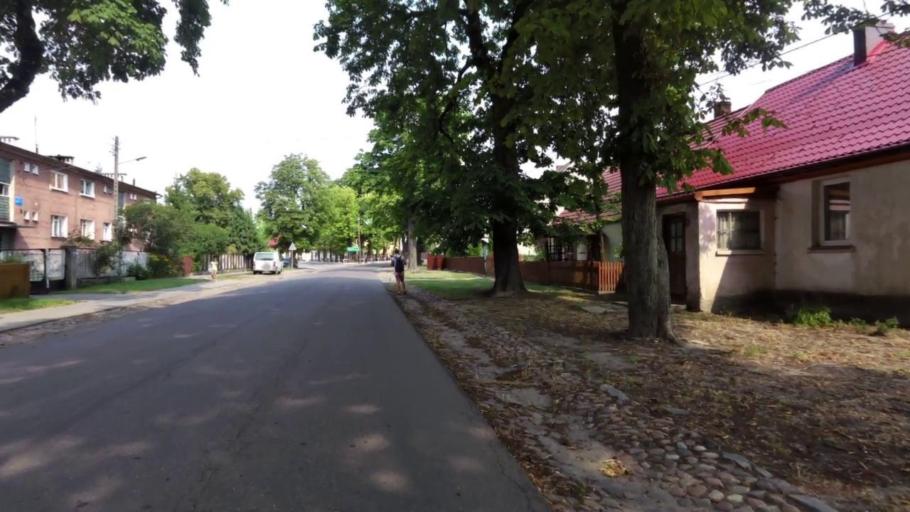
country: PL
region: West Pomeranian Voivodeship
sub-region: Powiat mysliborski
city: Debno
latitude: 52.8519
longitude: 14.6720
